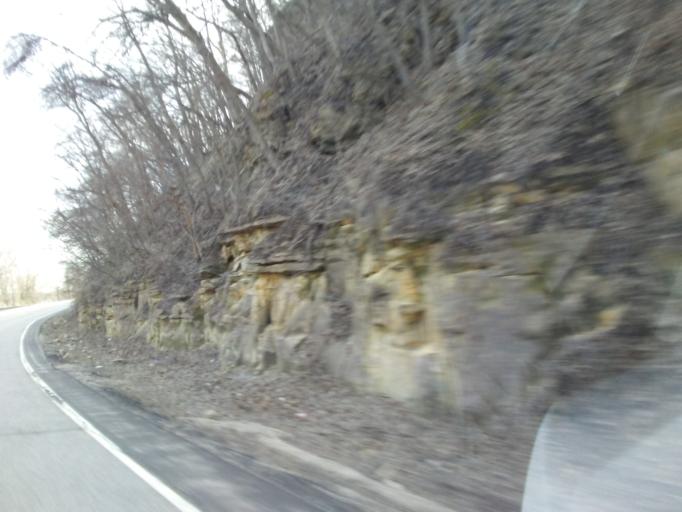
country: US
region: Wisconsin
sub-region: Crawford County
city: Prairie du Chien
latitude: 43.0846
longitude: -91.1810
